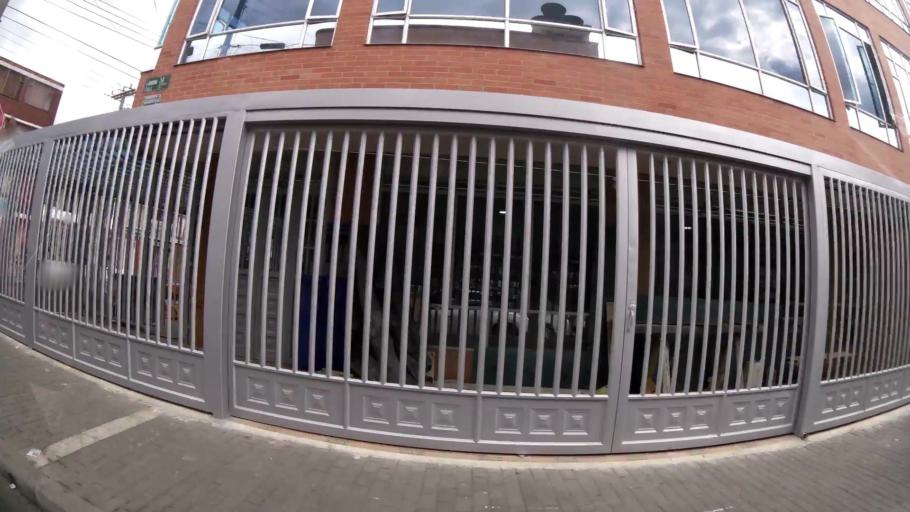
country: CO
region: Bogota D.C.
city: Bogota
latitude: 4.6042
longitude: -74.1314
